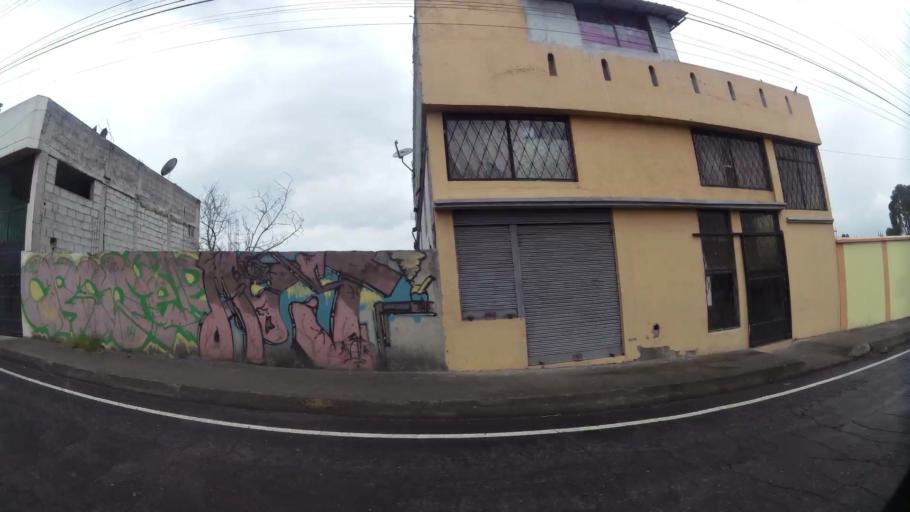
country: EC
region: Pichincha
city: Sangolqui
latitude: -0.3234
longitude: -78.4408
